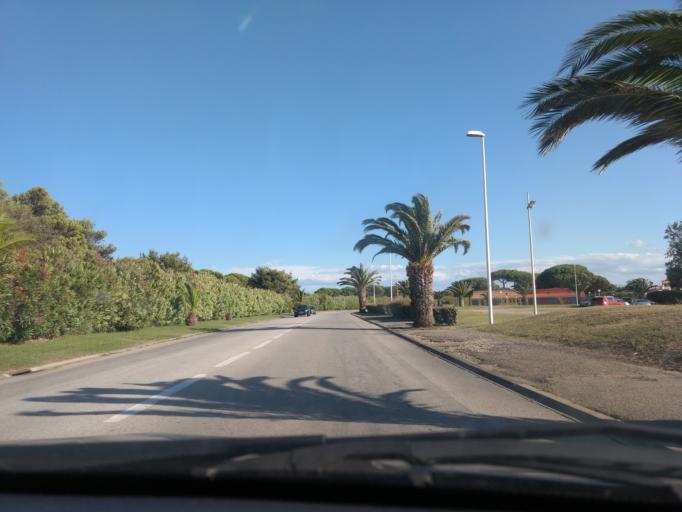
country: FR
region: Languedoc-Roussillon
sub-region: Departement des Pyrenees-Orientales
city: Le Barcares
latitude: 42.8137
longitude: 3.0296
